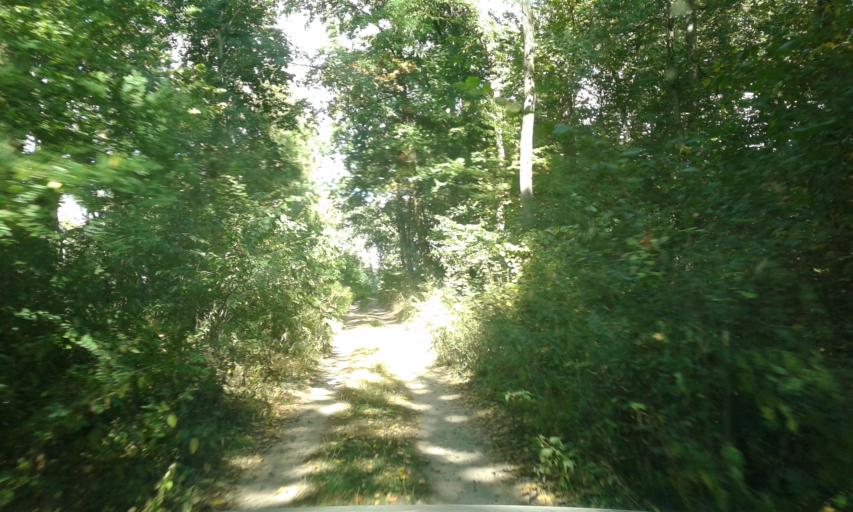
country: PL
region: West Pomeranian Voivodeship
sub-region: Powiat stargardzki
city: Suchan
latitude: 53.2050
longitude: 15.3253
